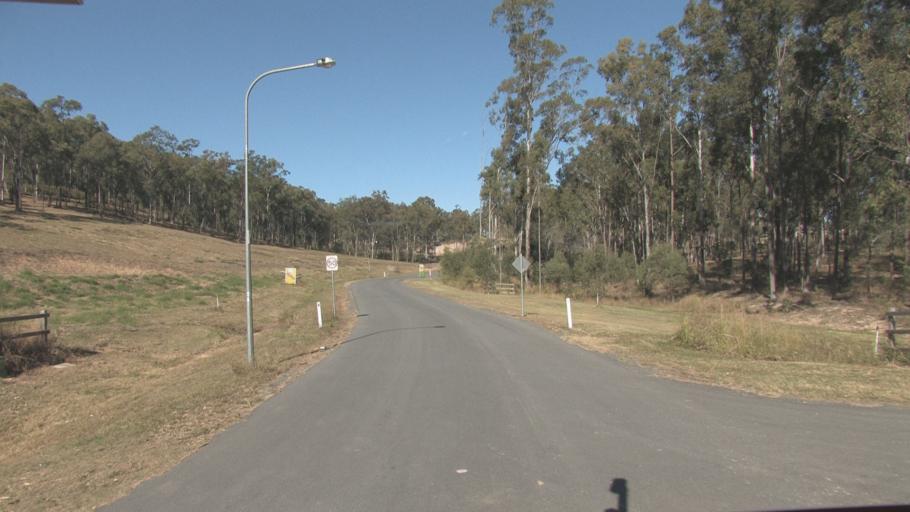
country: AU
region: Queensland
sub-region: Logan
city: Windaroo
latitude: -27.7725
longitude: 153.1459
